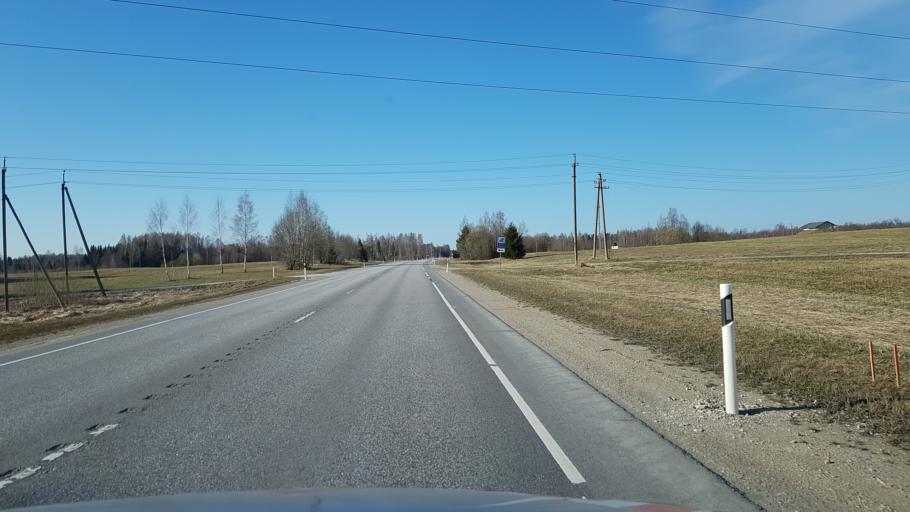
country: EE
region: Ida-Virumaa
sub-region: Johvi vald
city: Johvi
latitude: 59.1834
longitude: 27.3479
